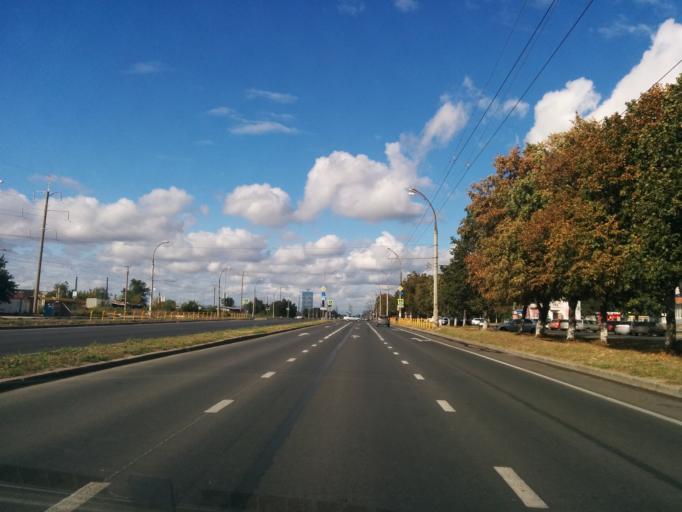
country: RU
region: Samara
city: Tol'yatti
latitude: 53.5356
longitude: 49.2631
